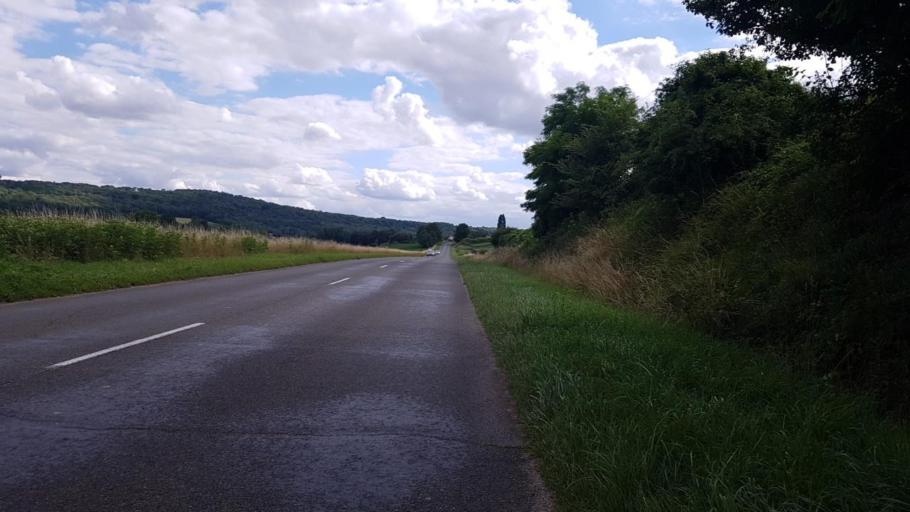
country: FR
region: Picardie
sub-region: Departement de l'Aisne
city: Crezancy
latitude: 49.0584
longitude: 3.4749
